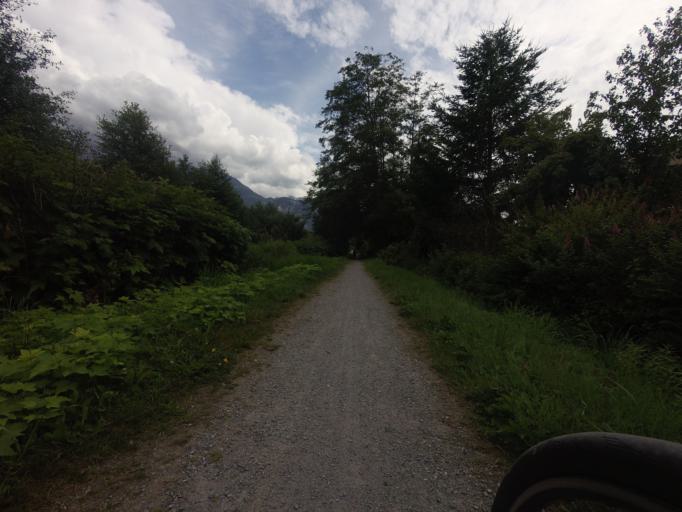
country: CA
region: British Columbia
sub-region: Greater Vancouver Regional District
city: Lions Bay
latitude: 49.7210
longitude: -123.1485
